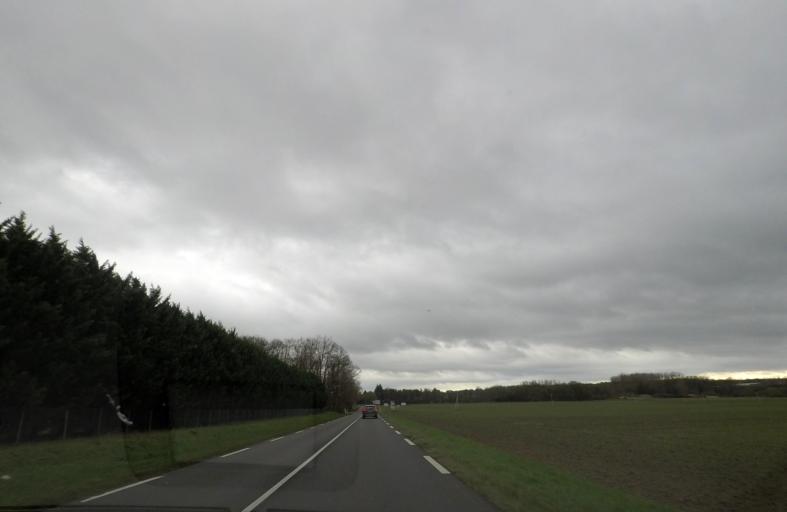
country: FR
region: Centre
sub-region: Departement du Loir-et-Cher
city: Cour-Cheverny
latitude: 47.5203
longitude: 1.4374
